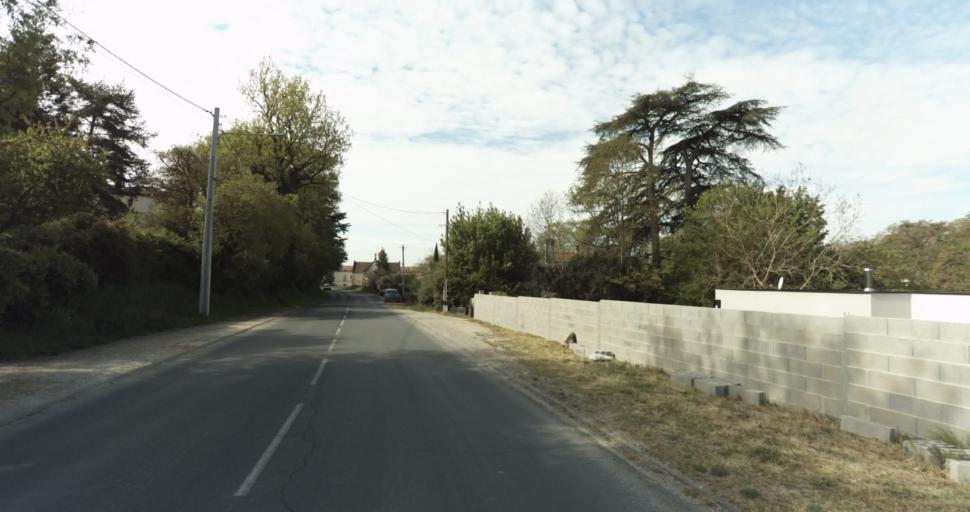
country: FR
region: Aquitaine
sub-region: Departement du Lot-et-Garonne
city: Le Passage
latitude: 44.2161
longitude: 0.6076
